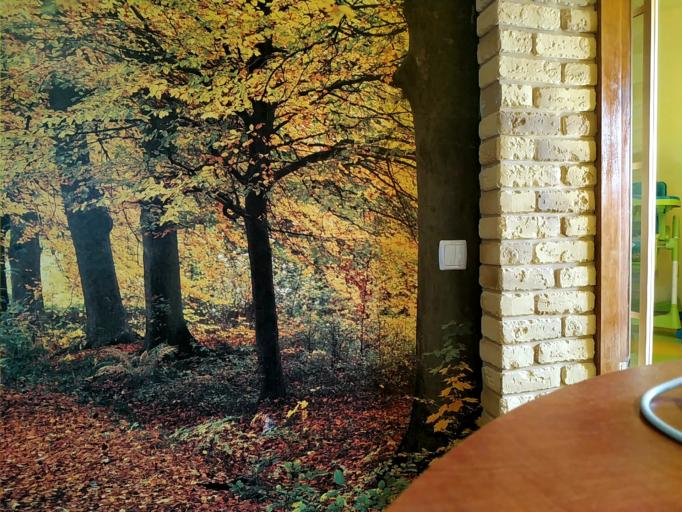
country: RU
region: Tverskaya
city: Kalashnikovo
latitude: 57.3356
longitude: 35.3193
